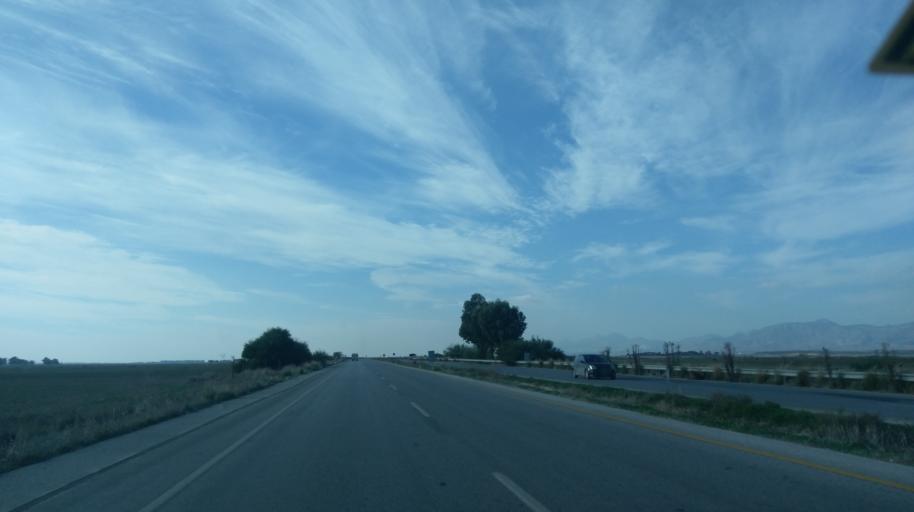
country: CY
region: Ammochostos
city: Lefkonoiko
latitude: 35.1874
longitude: 33.6365
